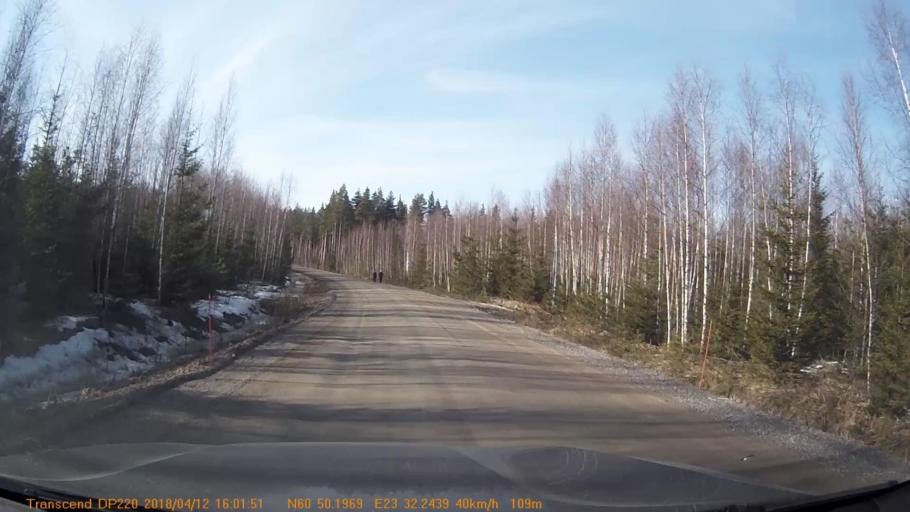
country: FI
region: Haeme
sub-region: Forssa
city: Jokioinen
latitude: 60.8370
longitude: 23.5369
